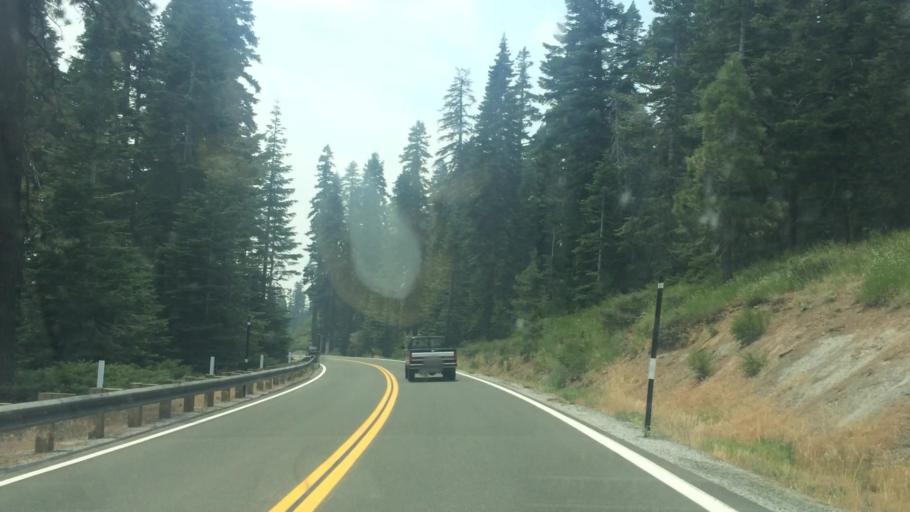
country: US
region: California
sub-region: Calaveras County
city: Arnold
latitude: 38.5771
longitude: -120.2604
